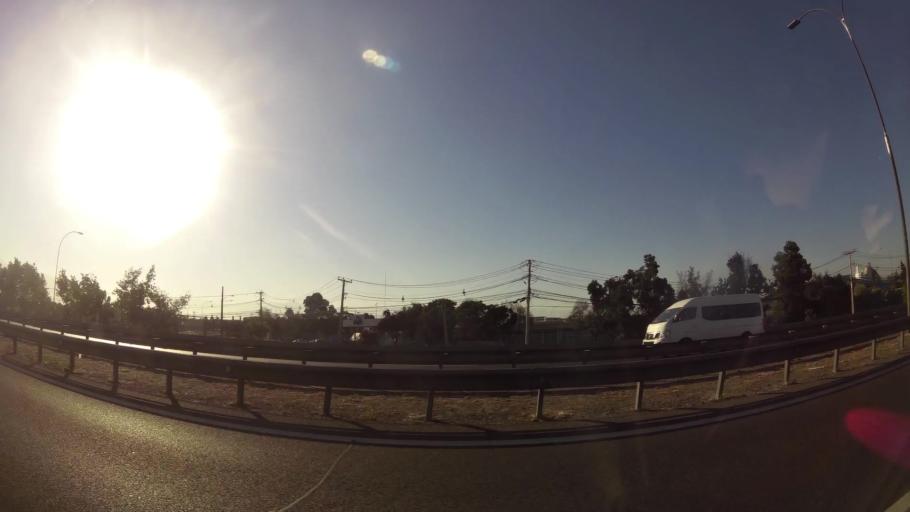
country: CL
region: Santiago Metropolitan
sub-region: Provincia de Maipo
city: San Bernardo
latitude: -33.5515
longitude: -70.7033
